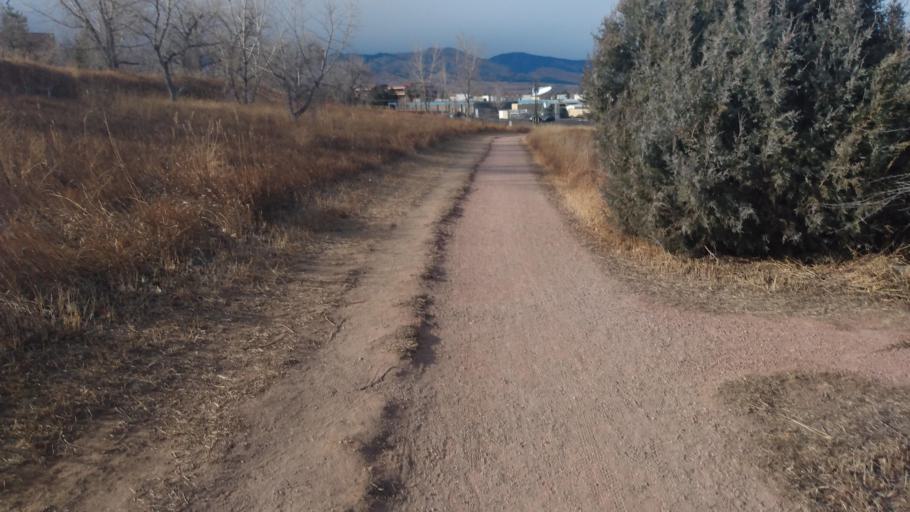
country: US
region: Colorado
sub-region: Boulder County
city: Gunbarrel
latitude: 40.0644
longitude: -105.2025
